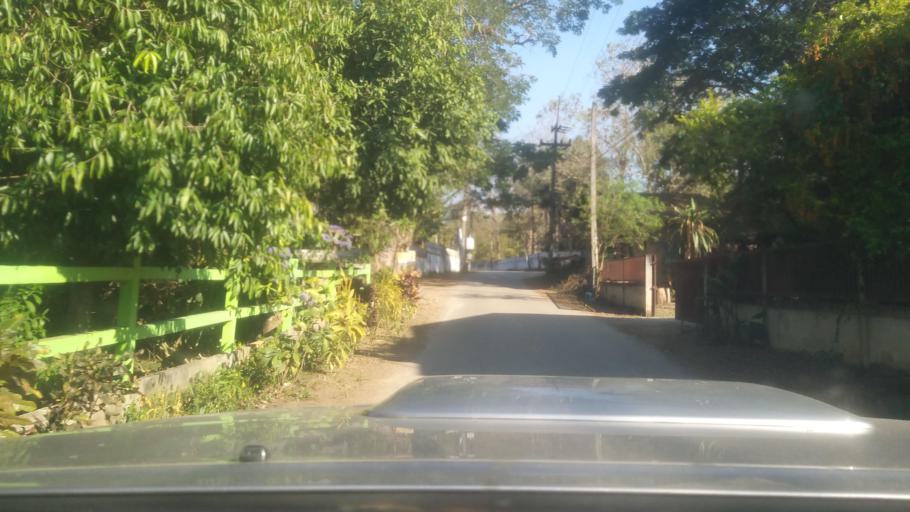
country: TH
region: Phrae
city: Phrae
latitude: 18.2608
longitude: 99.9977
